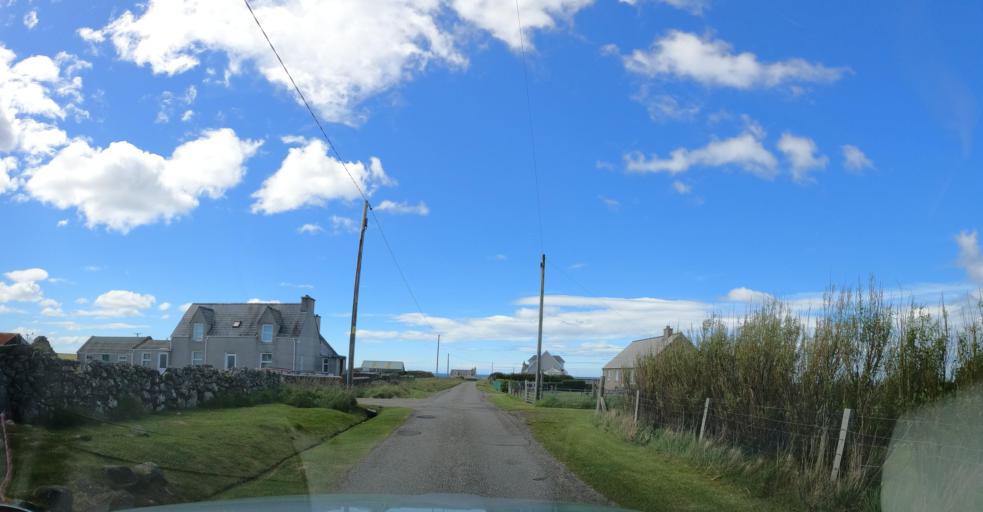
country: GB
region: Scotland
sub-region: Eilean Siar
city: Isle of Lewis
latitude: 58.3586
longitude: -6.5597
